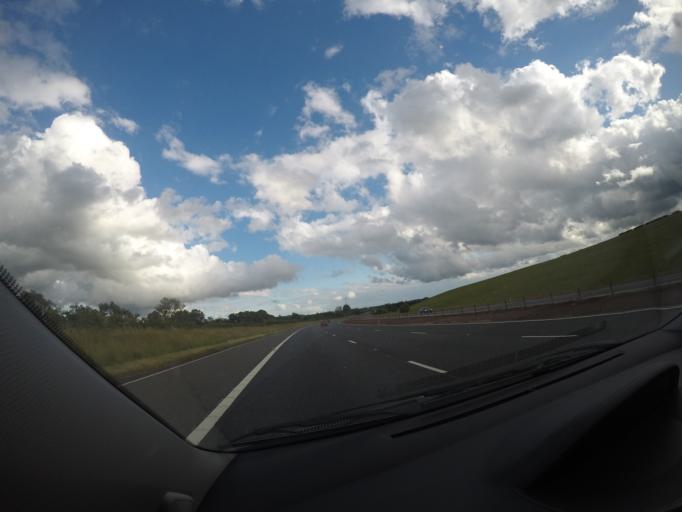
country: GB
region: Scotland
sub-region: Dumfries and Galloway
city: Lockerbie
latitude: 55.1664
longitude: -3.3889
